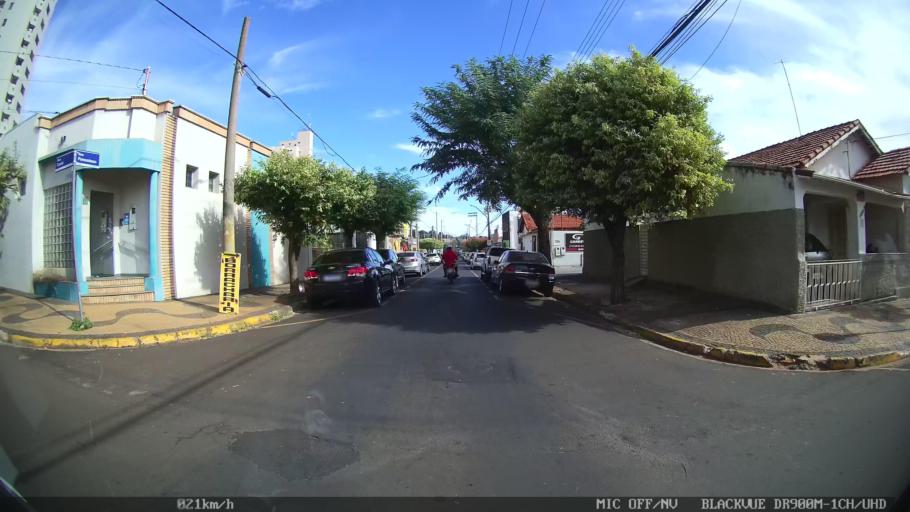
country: BR
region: Sao Paulo
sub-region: Catanduva
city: Catanduva
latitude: -21.1336
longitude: -48.9746
